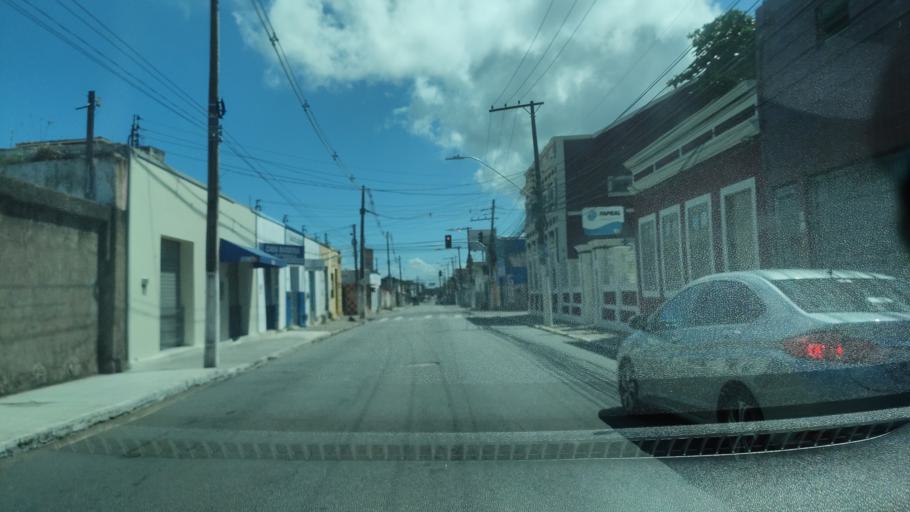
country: BR
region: Alagoas
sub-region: Maceio
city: Maceio
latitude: -9.6612
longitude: -35.7414
